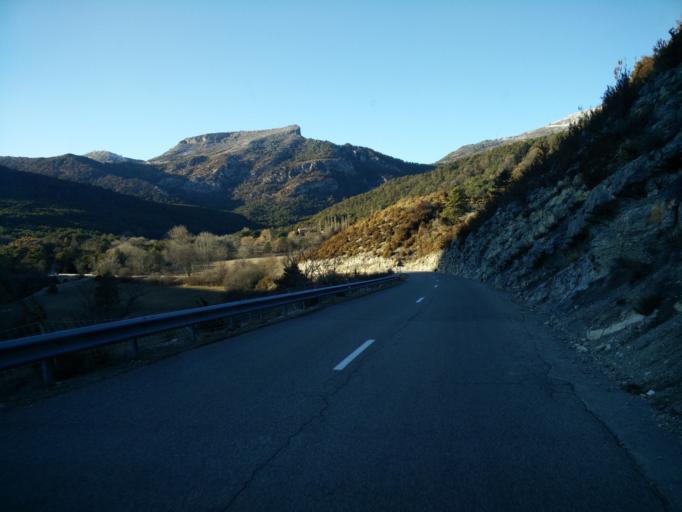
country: FR
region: Provence-Alpes-Cote d'Azur
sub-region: Departement des Alpes-de-Haute-Provence
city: Castellane
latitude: 43.7919
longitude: 6.3824
